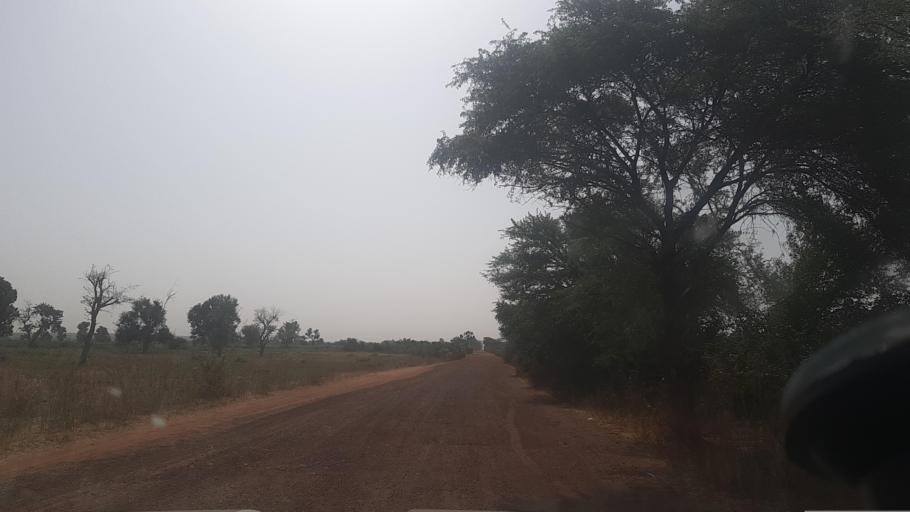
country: ML
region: Segou
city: Baroueli
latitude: 13.1439
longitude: -6.5152
